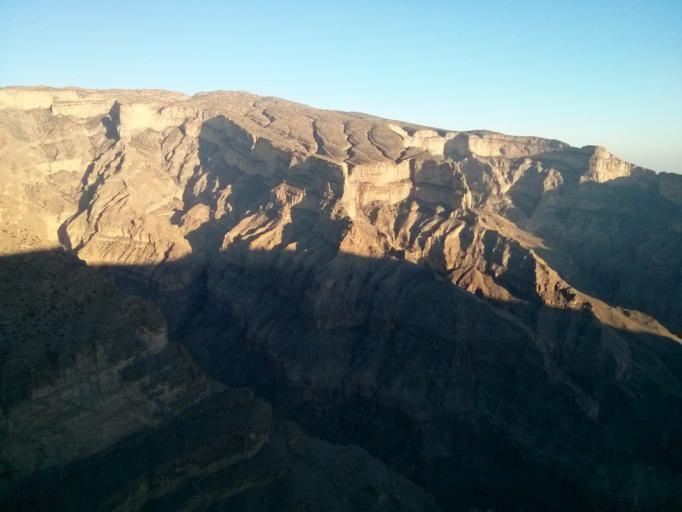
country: OM
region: Muhafazat ad Dakhiliyah
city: Nizwa
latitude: 22.9331
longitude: 57.5308
